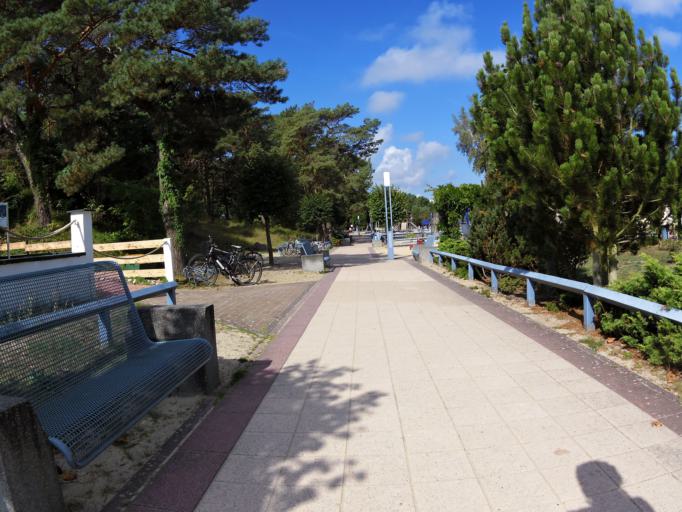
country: DE
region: Mecklenburg-Vorpommern
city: Ostseebad Zinnowitz
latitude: 54.0966
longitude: 13.8786
